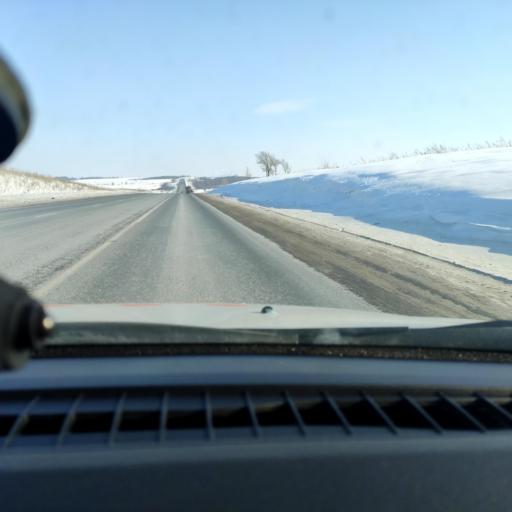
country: RU
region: Samara
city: Novosemeykino
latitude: 53.4026
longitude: 50.3937
